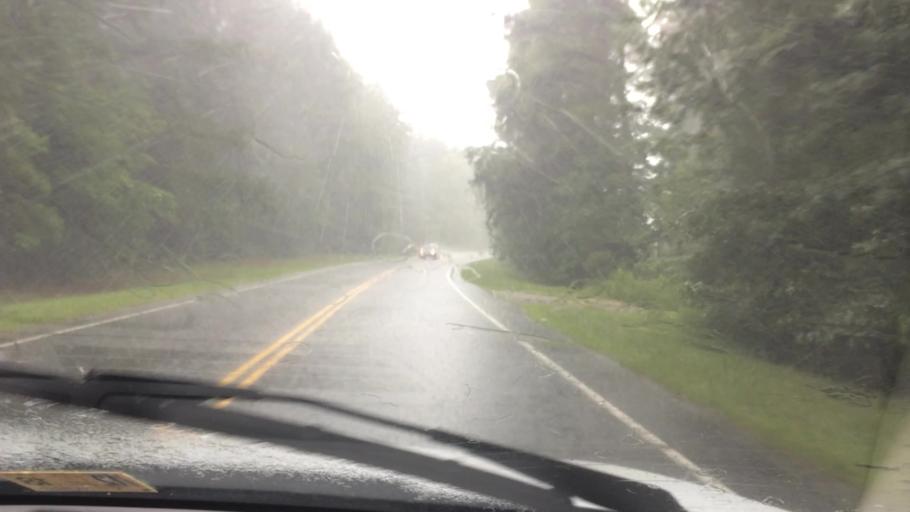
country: US
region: Virginia
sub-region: James City County
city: Williamsburg
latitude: 37.3854
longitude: -76.7658
